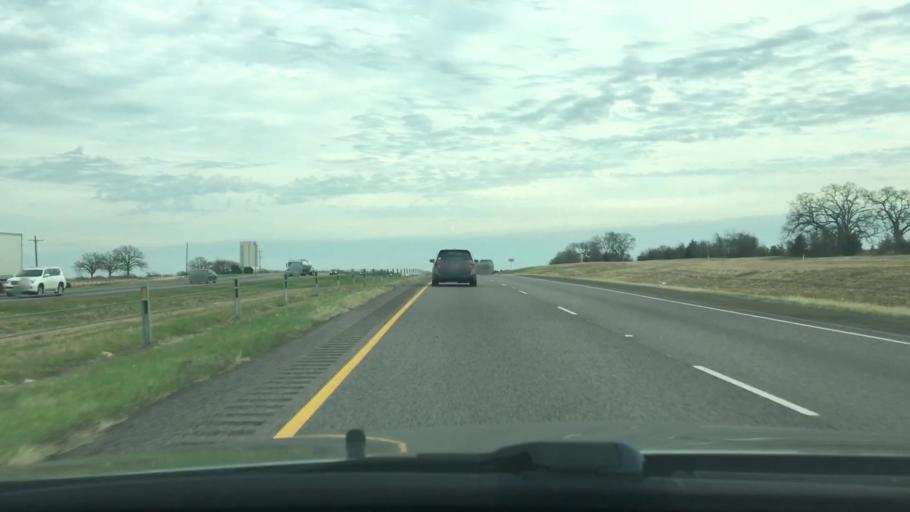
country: US
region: Texas
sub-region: Madison County
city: Madisonville
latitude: 30.9515
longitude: -95.8635
